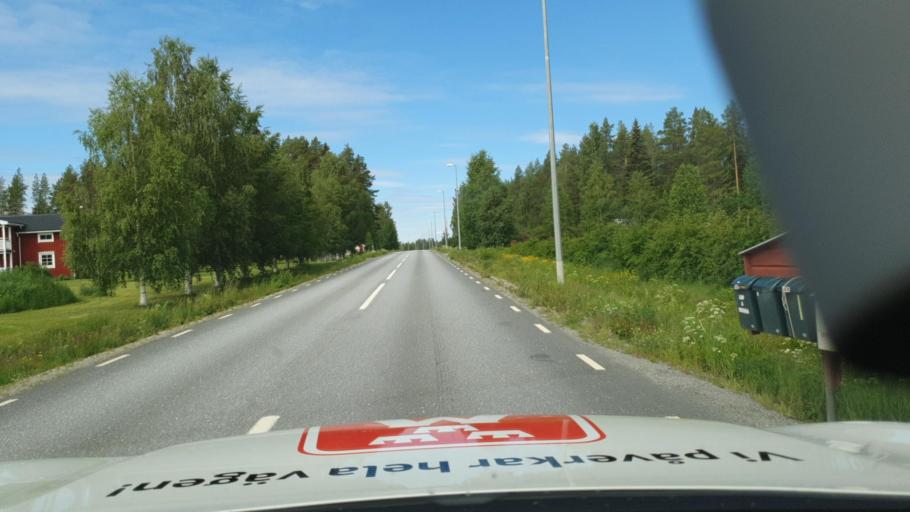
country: SE
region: Vaesterbotten
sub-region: Skelleftea Kommun
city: Forsbacka
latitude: 64.6923
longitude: 20.4992
